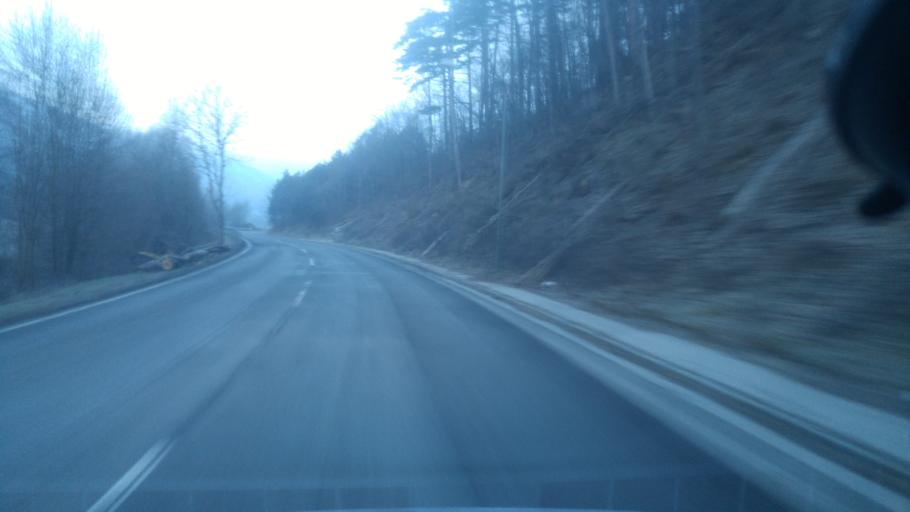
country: AT
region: Lower Austria
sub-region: Politischer Bezirk Baden
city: Pottenstein
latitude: 47.9699
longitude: 16.0795
